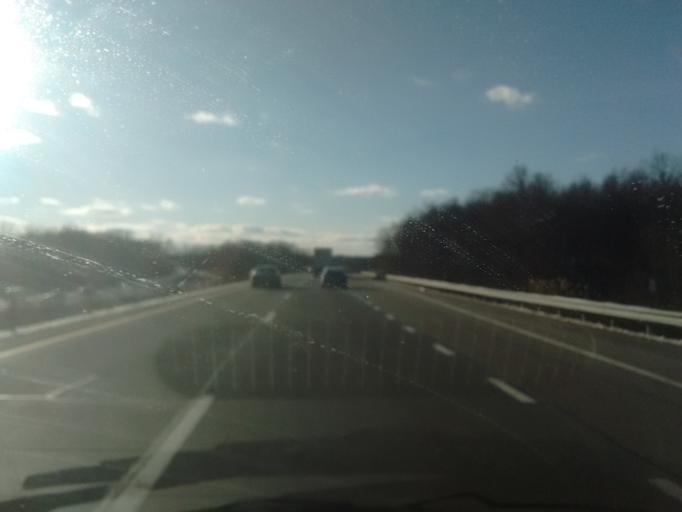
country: US
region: New York
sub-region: Orange County
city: Orange Lake
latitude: 41.5142
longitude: -74.1227
